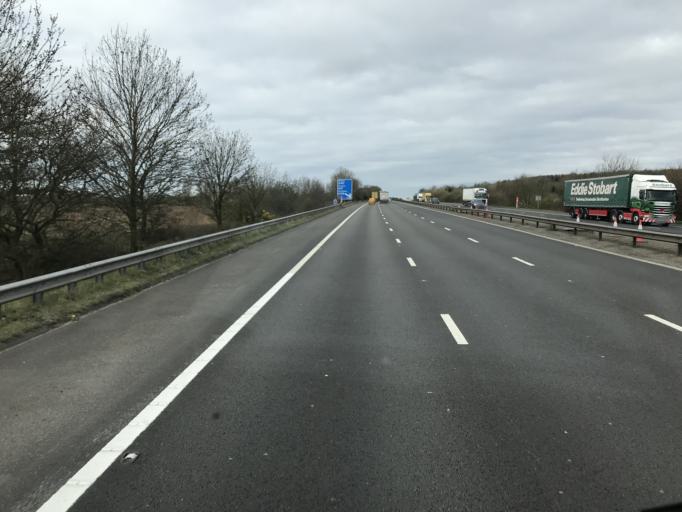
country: GB
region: England
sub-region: St. Helens
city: St Helens
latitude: 53.4094
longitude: -2.7090
